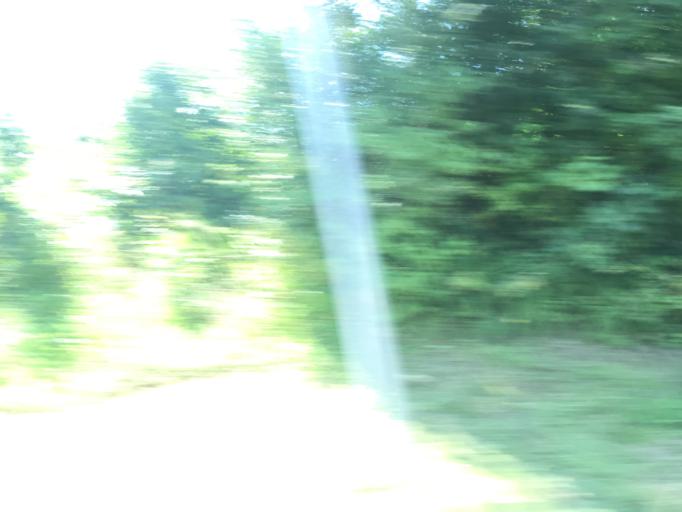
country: SI
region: Metlika
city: Metlika
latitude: 45.6085
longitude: 15.3304
